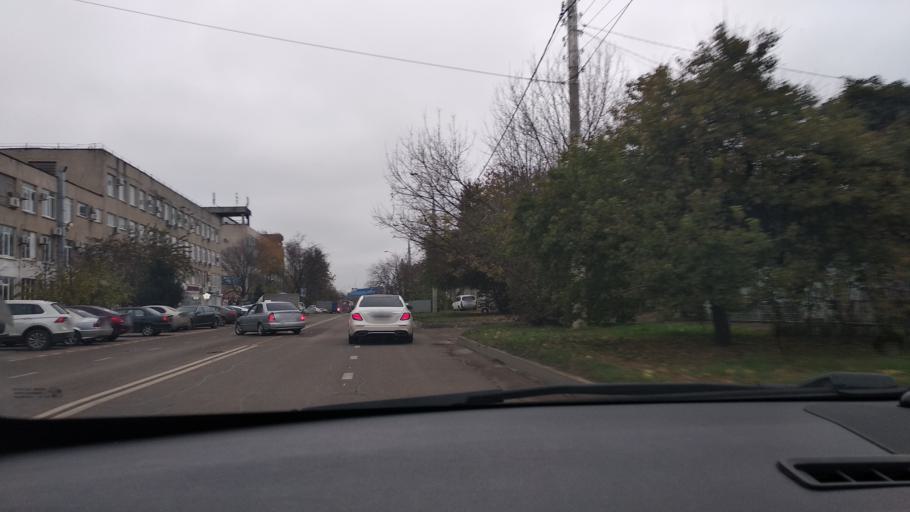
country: RU
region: Krasnodarskiy
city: Krasnodar
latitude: 45.0282
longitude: 39.0200
